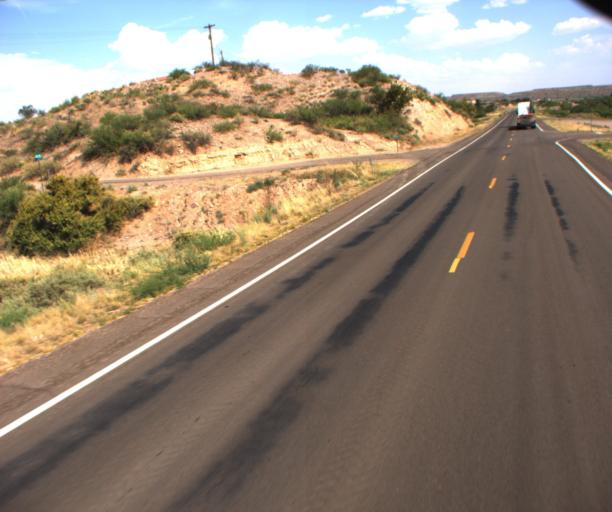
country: US
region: Arizona
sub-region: Greenlee County
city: Clifton
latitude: 32.8712
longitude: -109.1908
